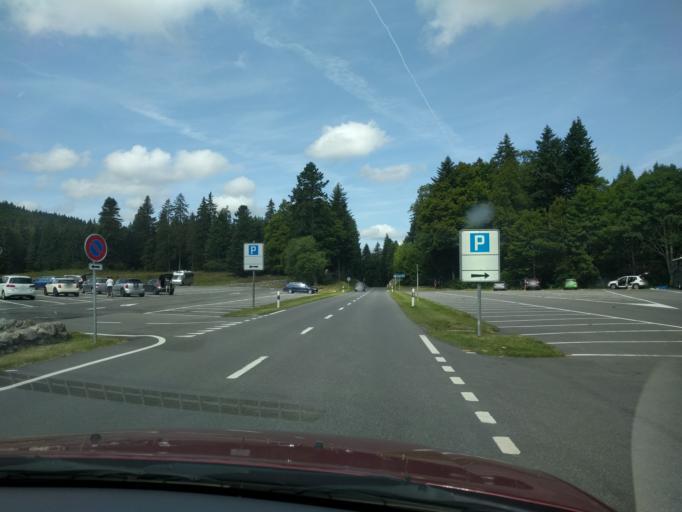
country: CH
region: Vaud
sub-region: Jura-Nord vaudois District
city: L'Abbaye
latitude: 46.6498
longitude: 6.3661
